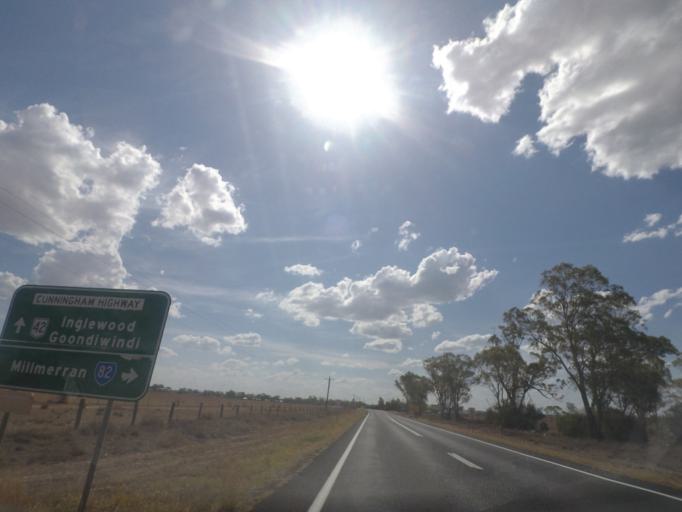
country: AU
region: New South Wales
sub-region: Moree Plains
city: Boggabilla
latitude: -28.4113
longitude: 151.1011
